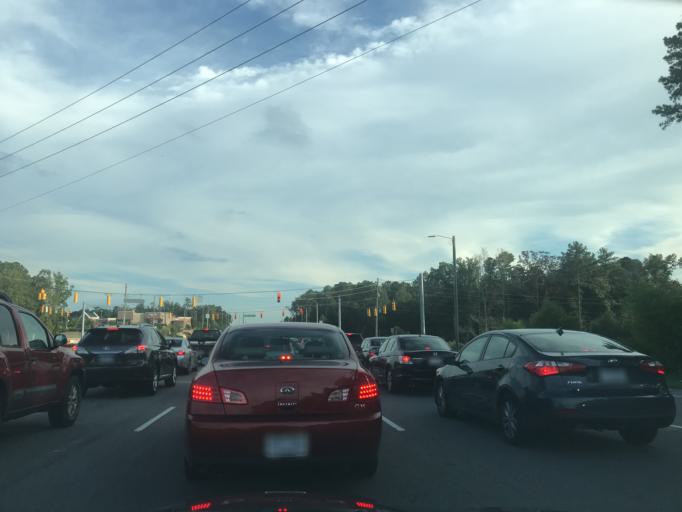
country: US
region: North Carolina
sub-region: Wake County
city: Green Level
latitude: 35.8465
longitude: -78.8916
